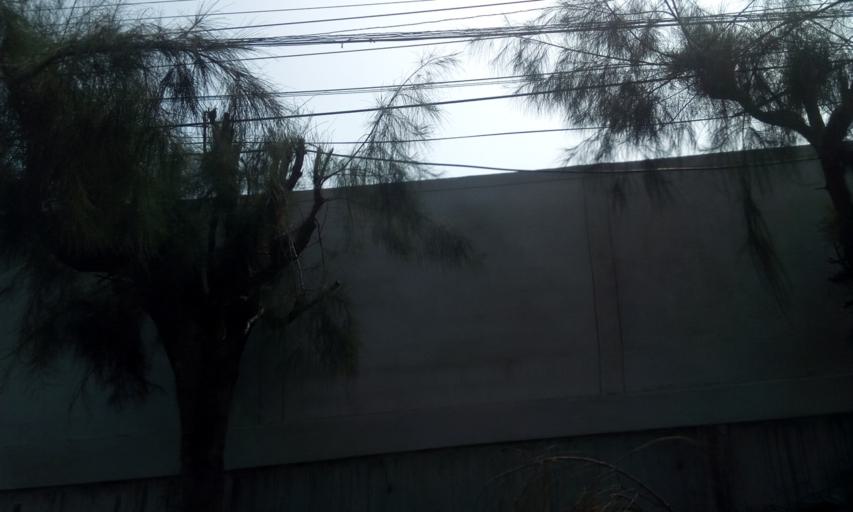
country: TH
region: Pathum Thani
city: Ban Lam Luk Ka
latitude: 13.9716
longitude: 100.7516
